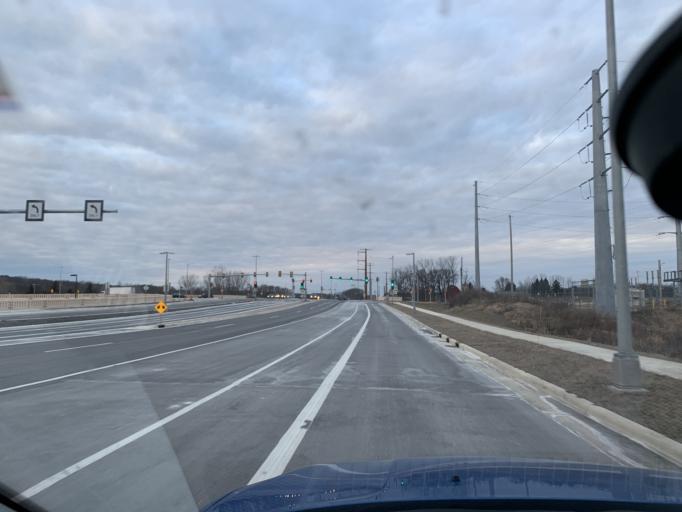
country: US
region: Wisconsin
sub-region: Dane County
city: Verona
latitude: 43.0146
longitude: -89.5333
